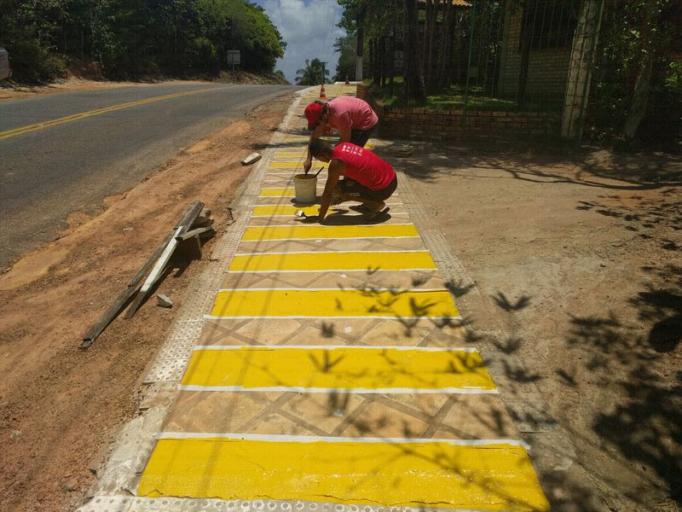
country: BR
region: Rio Grande do Norte
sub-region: Ares
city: Ares
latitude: -6.2264
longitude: -35.0655
